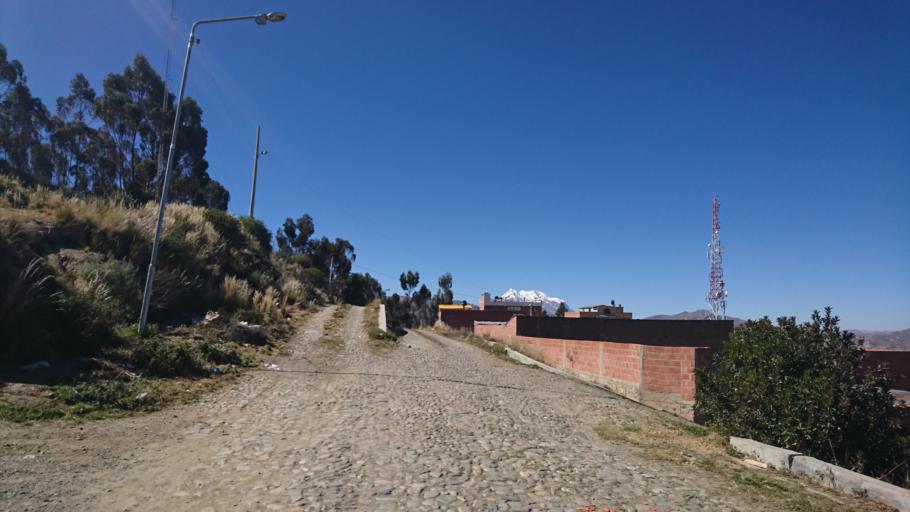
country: BO
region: La Paz
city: La Paz
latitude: -16.4868
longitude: -68.1042
